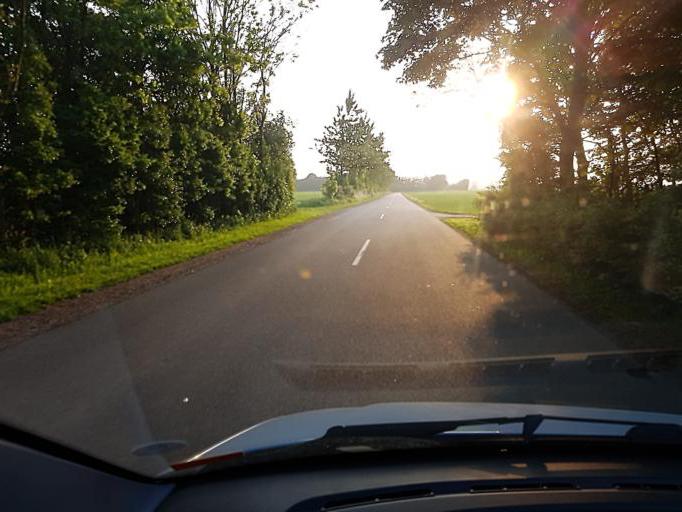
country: DK
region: South Denmark
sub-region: Esbjerg Kommune
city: Tjaereborg
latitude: 55.5473
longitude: 8.5633
